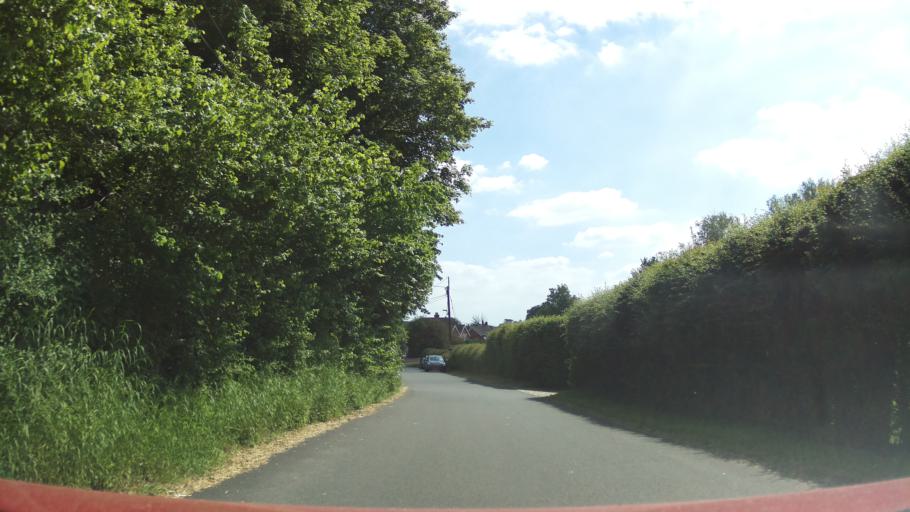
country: GB
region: England
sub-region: Wiltshire
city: Rushall
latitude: 51.2640
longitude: -1.7965
